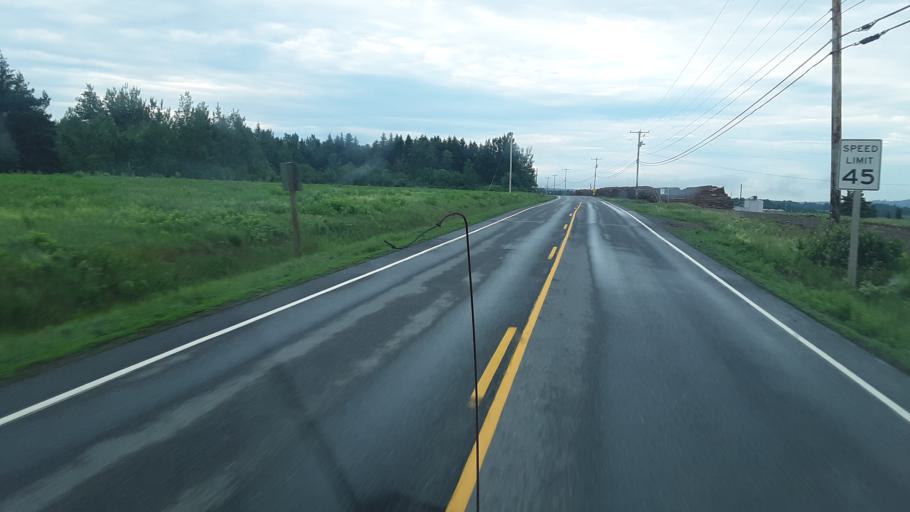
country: US
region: Maine
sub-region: Aroostook County
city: Presque Isle
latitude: 46.5371
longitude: -68.3620
